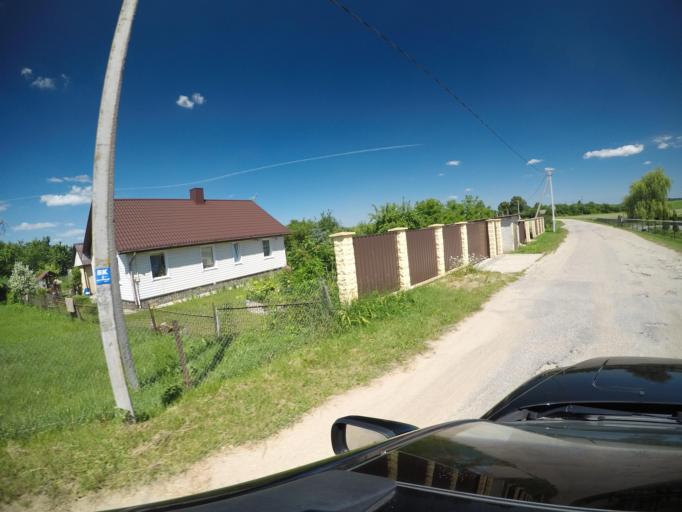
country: BY
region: Grodnenskaya
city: Hrodna
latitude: 53.7285
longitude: 23.8508
